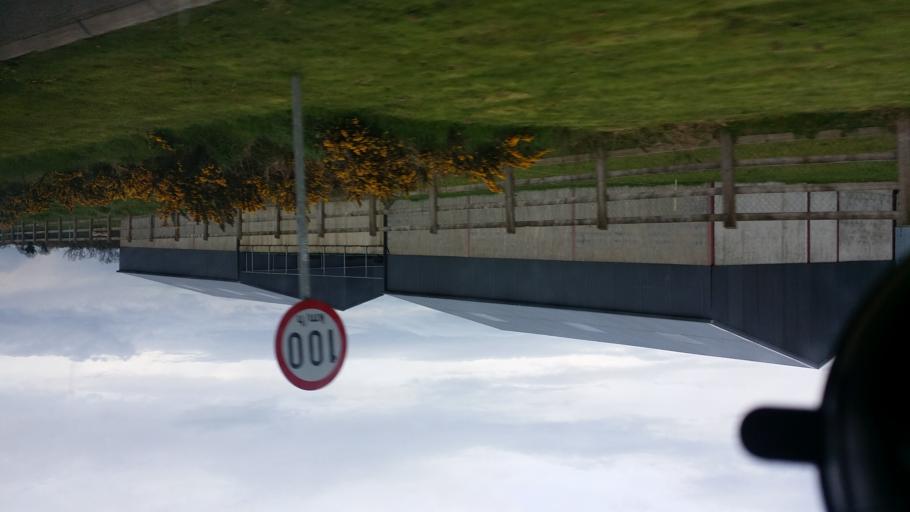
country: IE
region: Ulster
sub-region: An Cabhan
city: Belturbet
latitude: 54.0977
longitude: -7.4601
